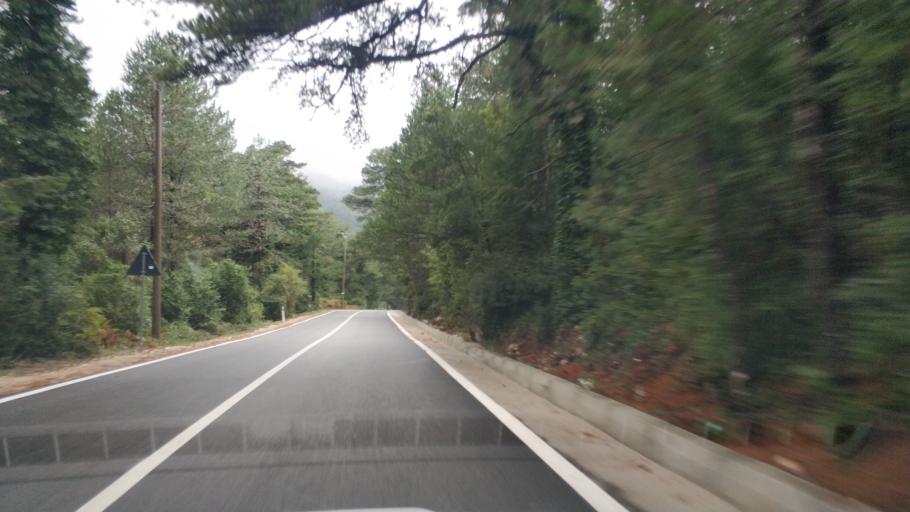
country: AL
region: Vlore
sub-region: Rrethi i Vlores
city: Brataj
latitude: 40.2068
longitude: 19.5848
